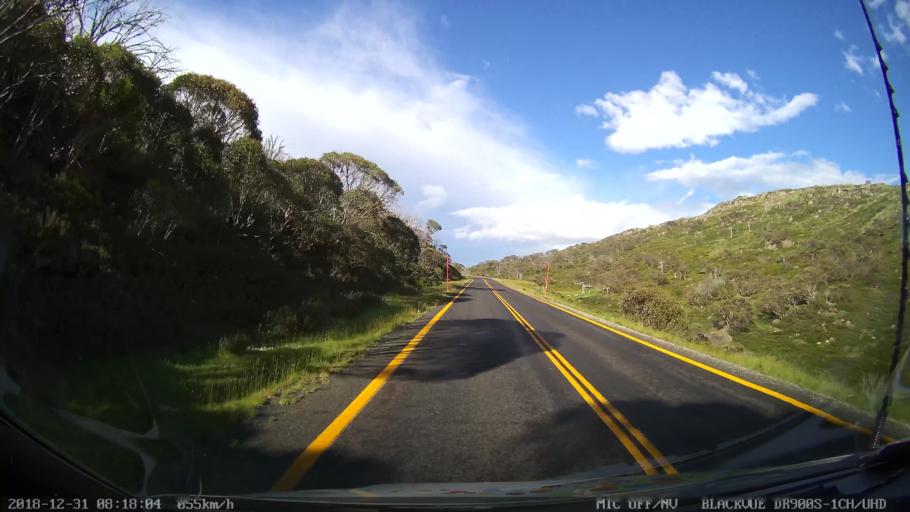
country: AU
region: New South Wales
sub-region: Snowy River
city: Jindabyne
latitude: -36.4125
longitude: 148.3985
